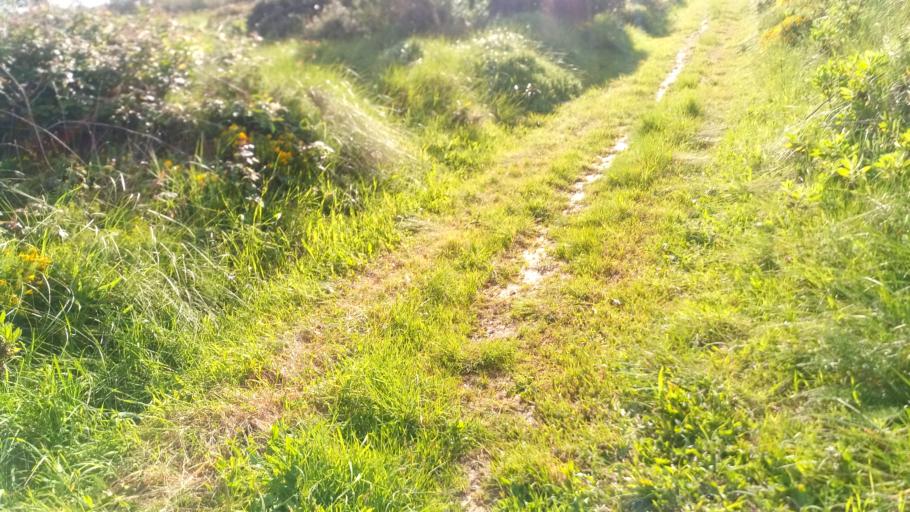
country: PT
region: Leiria
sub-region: Caldas da Rainha
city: Caldas da Rainha
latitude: 39.4492
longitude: -9.1941
